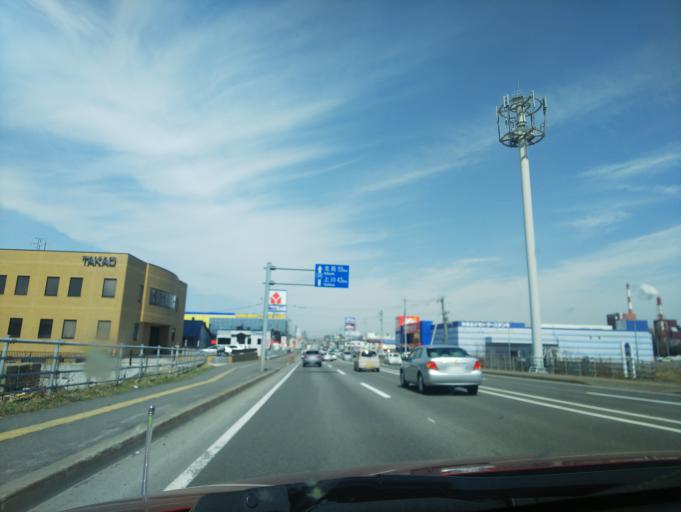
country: JP
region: Hokkaido
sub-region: Asahikawa-shi
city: Asahikawa
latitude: 43.7724
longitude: 142.3821
